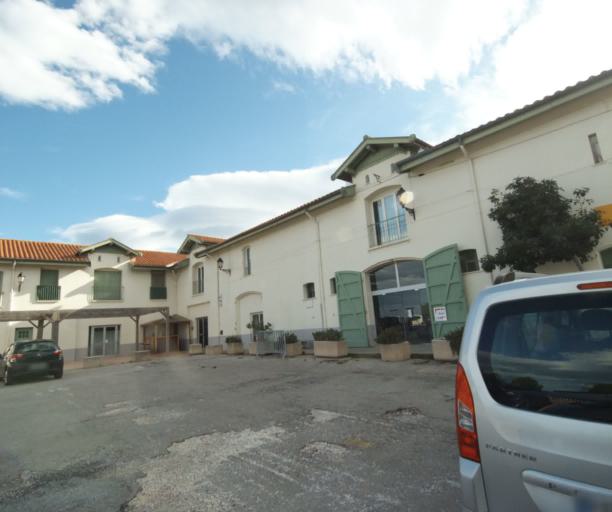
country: FR
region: Languedoc-Roussillon
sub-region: Departement des Pyrenees-Orientales
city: Argelers
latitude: 42.5312
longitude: 3.0300
